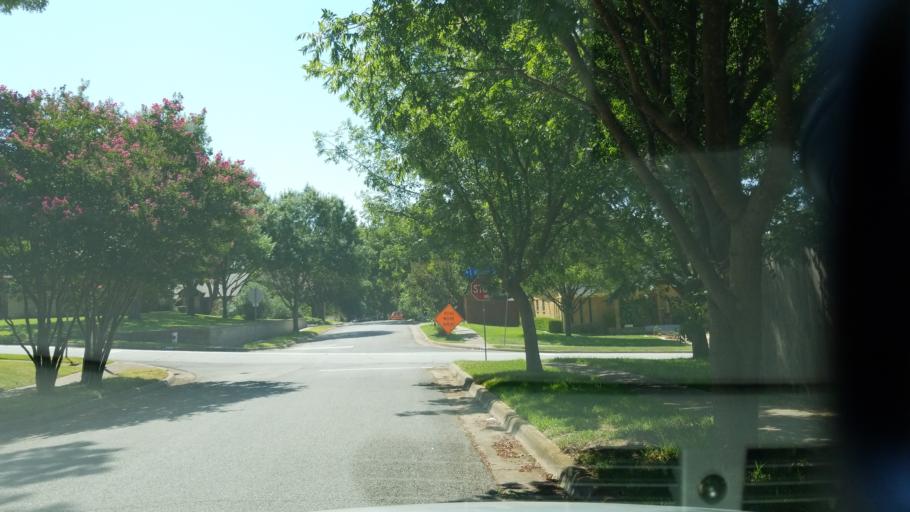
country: US
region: Texas
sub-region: Dallas County
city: Duncanville
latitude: 32.6505
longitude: -96.8978
